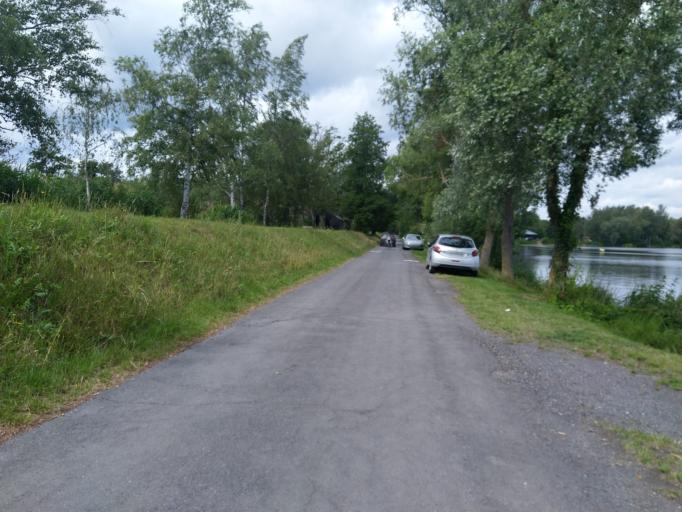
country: FR
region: Nord-Pas-de-Calais
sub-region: Departement du Nord
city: Conde-sur-l'Escaut
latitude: 50.4498
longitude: 3.6045
